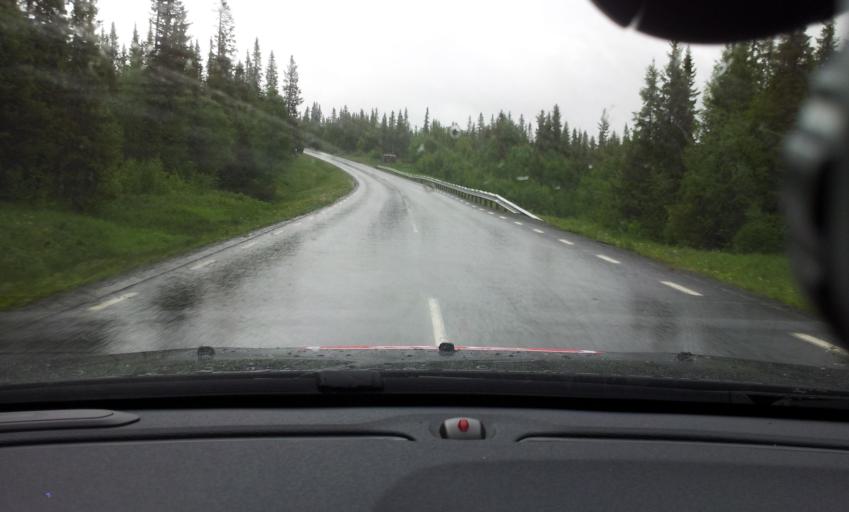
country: SE
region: Jaemtland
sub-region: Are Kommun
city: Are
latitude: 63.2572
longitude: 13.2107
